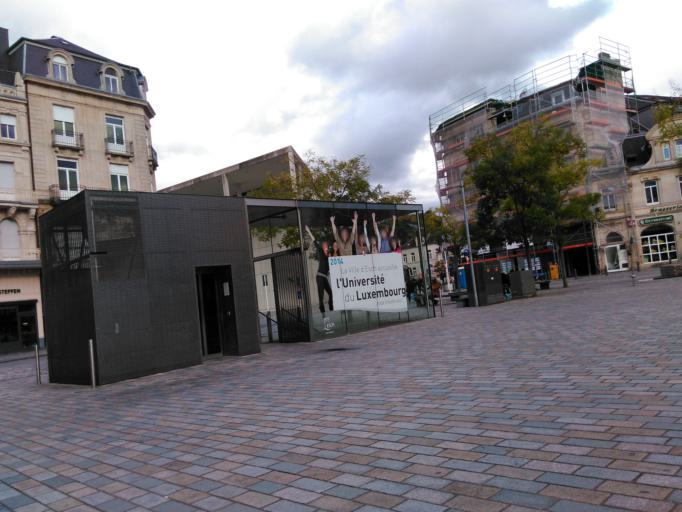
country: LU
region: Luxembourg
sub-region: Canton d'Esch-sur-Alzette
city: Esch-sur-Alzette
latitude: 49.4962
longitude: 5.9850
